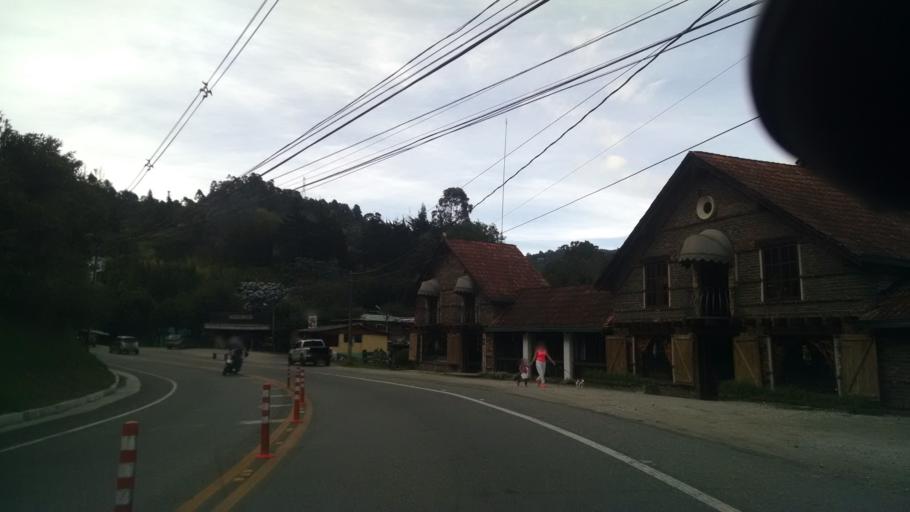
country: CO
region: Antioquia
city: El Retiro
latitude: 6.1193
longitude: -75.5006
